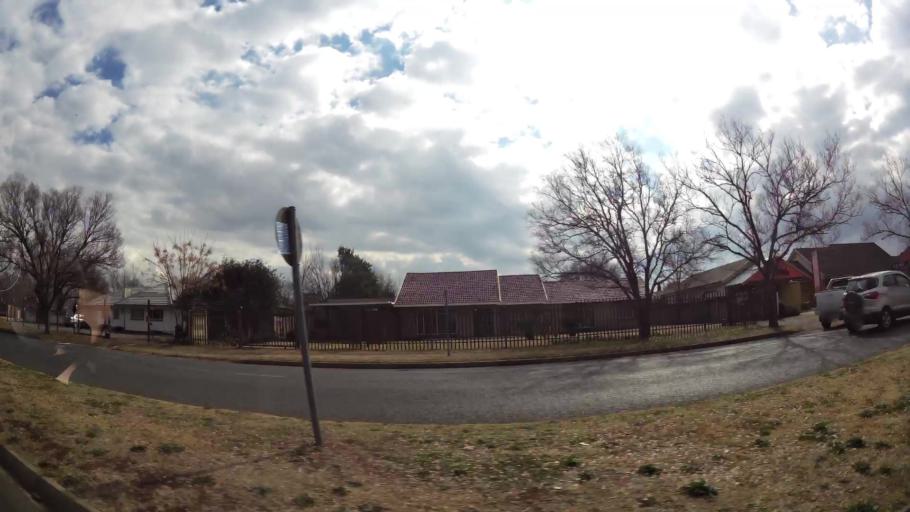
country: ZA
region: Gauteng
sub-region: Sedibeng District Municipality
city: Vereeniging
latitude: -26.6602
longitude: 27.9832
